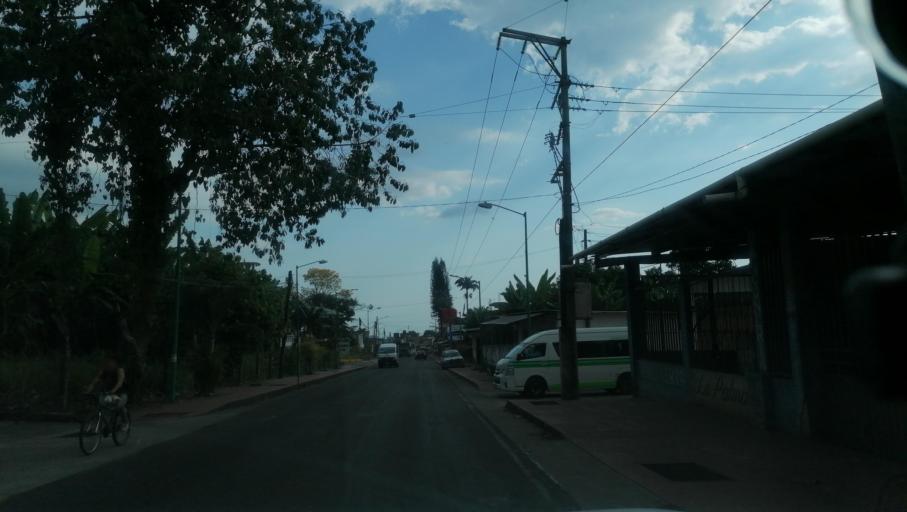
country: MX
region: Chiapas
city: Cacahoatan
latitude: 15.0005
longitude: -92.1630
